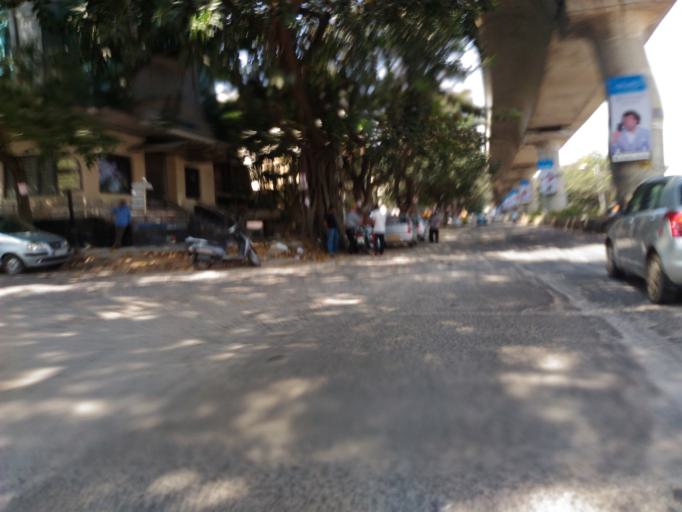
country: IN
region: Karnataka
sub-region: Bangalore Urban
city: Bangalore
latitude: 12.9406
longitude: 77.5801
